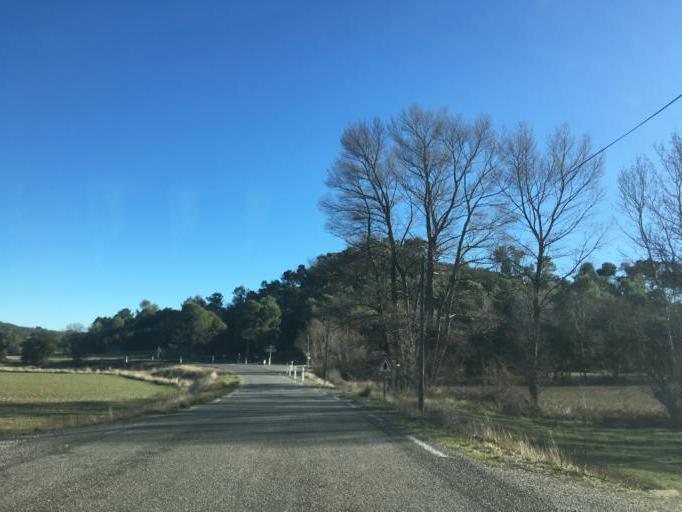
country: FR
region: Provence-Alpes-Cote d'Azur
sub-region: Departement du Var
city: Barjols
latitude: 43.5928
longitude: 6.0757
